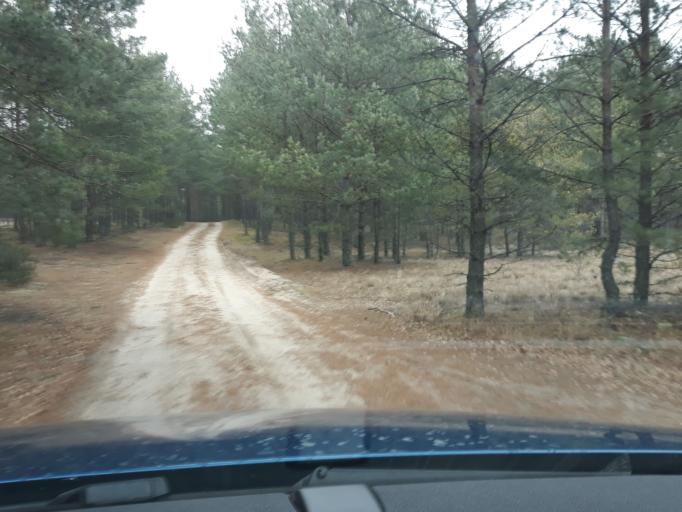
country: PL
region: Pomeranian Voivodeship
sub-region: Powiat chojnicki
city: Chojnice
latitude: 53.8578
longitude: 17.5405
